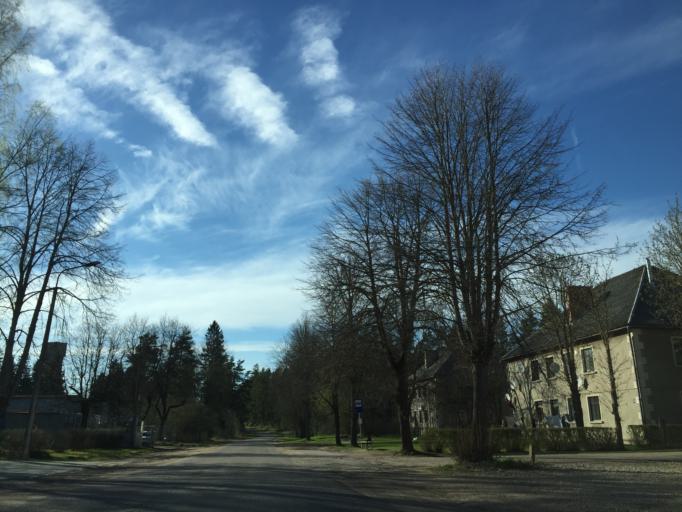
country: LV
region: Valkas Rajons
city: Valka
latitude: 57.7866
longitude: 25.9960
